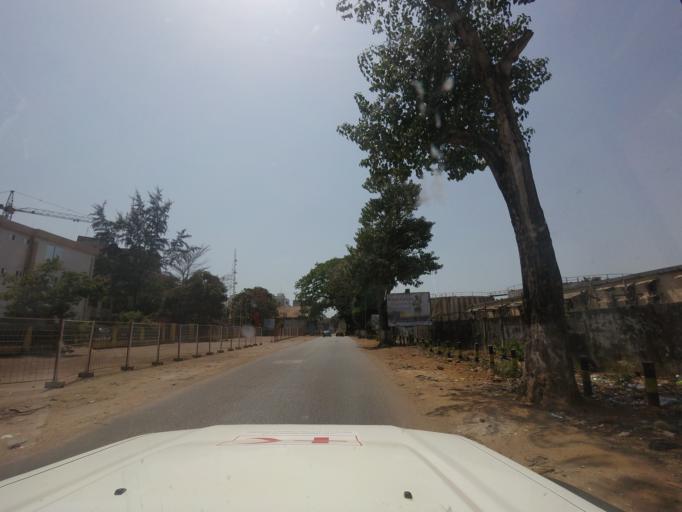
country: GN
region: Conakry
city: Camayenne
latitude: 9.5155
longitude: -13.7084
